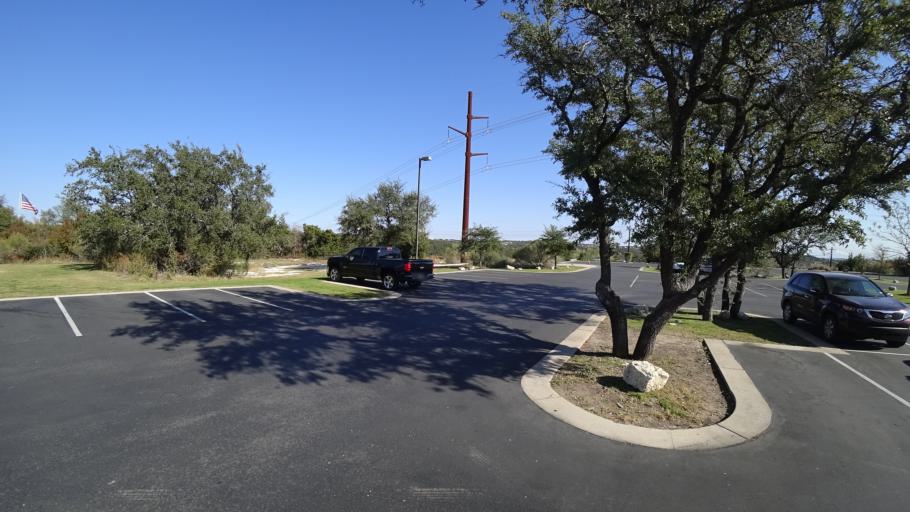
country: US
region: Texas
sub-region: Travis County
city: Hudson Bend
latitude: 30.3901
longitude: -97.8714
